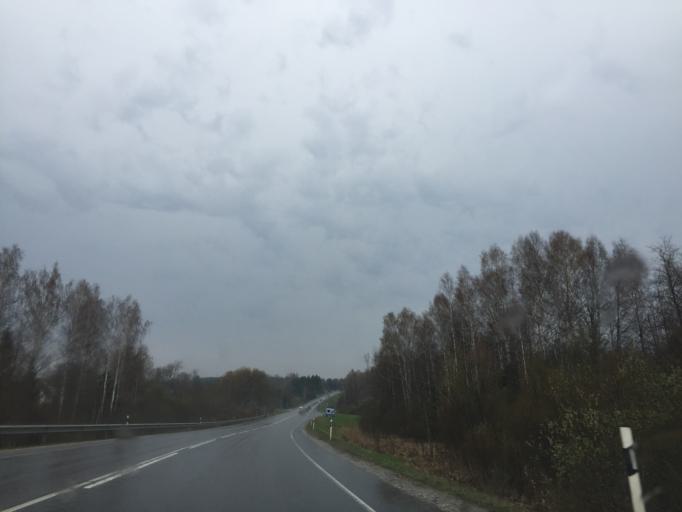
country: EE
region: Tartu
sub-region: UElenurme vald
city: Ulenurme
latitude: 58.2498
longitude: 26.6785
